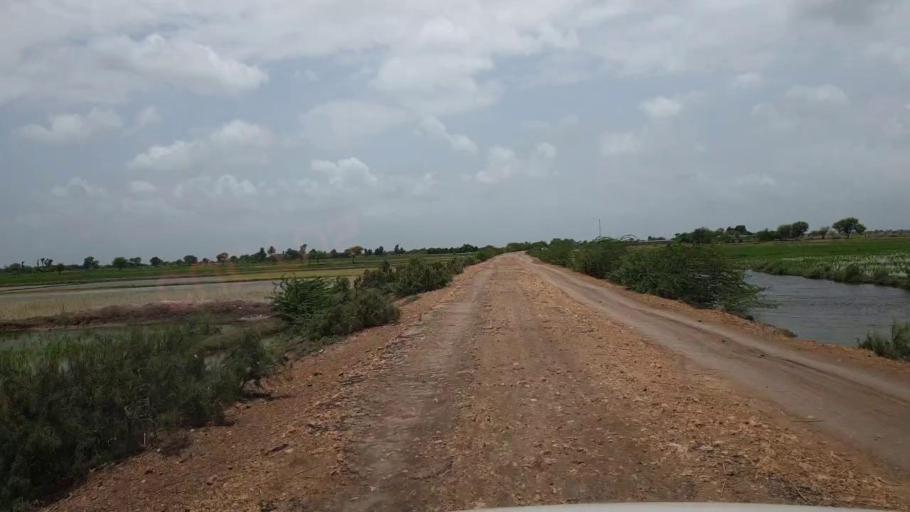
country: PK
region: Sindh
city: Kario
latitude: 24.7201
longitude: 68.5722
